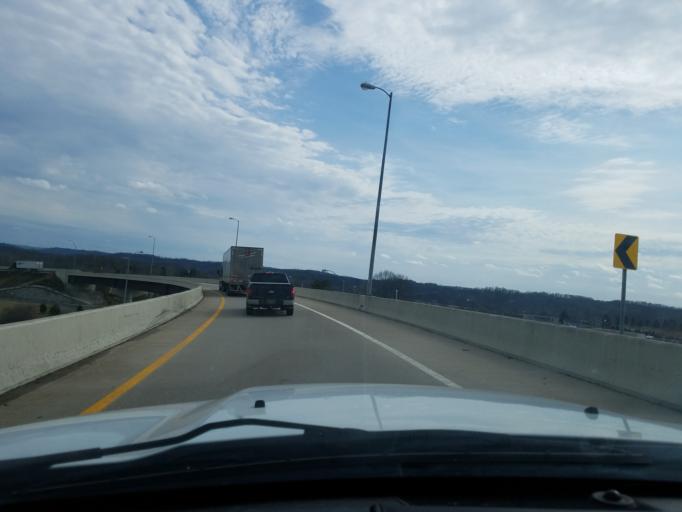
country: US
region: West Virginia
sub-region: Putnam County
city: Teays Valley
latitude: 38.4542
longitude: -81.9042
